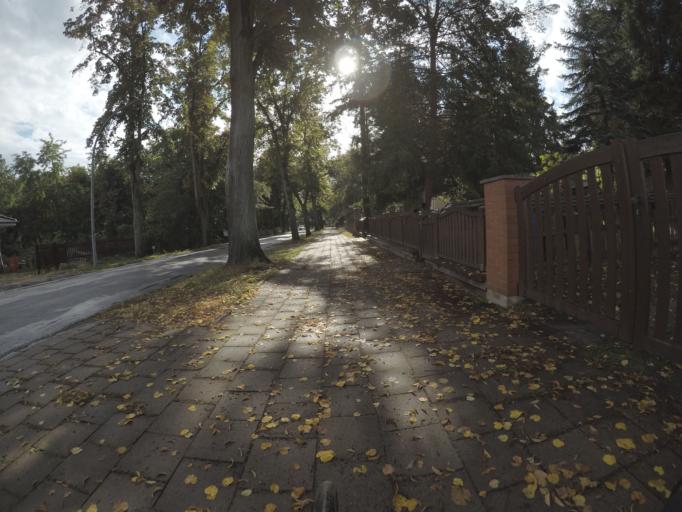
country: DE
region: Brandenburg
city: Strausberg
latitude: 52.5422
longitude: 13.8552
